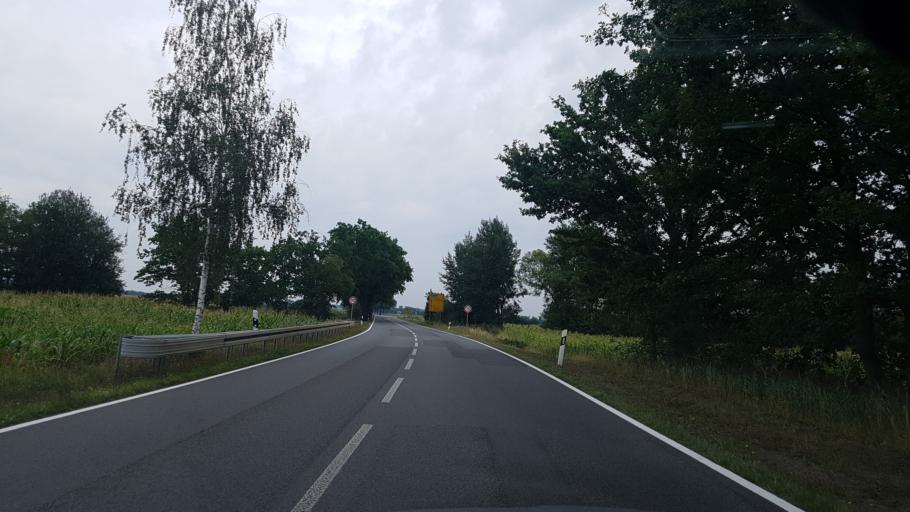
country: DE
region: Brandenburg
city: Schraden
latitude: 51.4664
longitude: 13.7085
